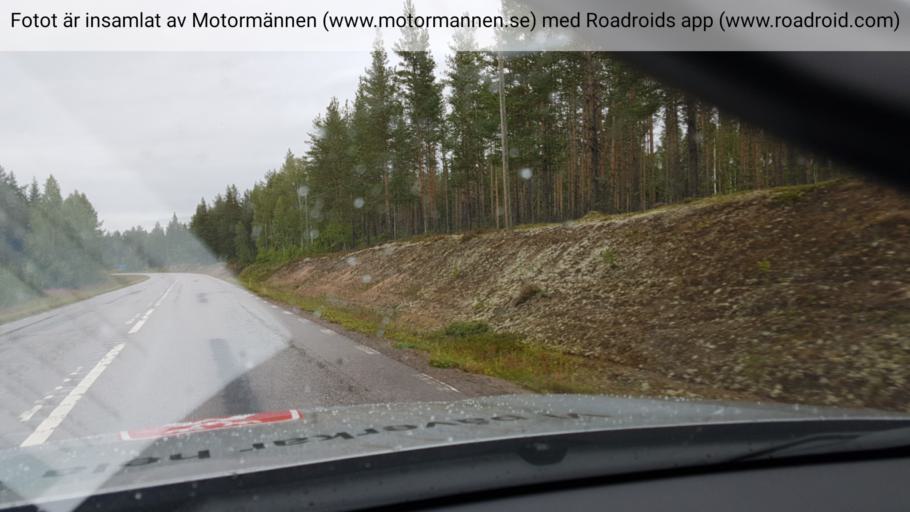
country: SE
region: Norrbotten
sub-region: Alvsbyns Kommun
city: AElvsbyn
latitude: 66.2249
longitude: 20.8753
